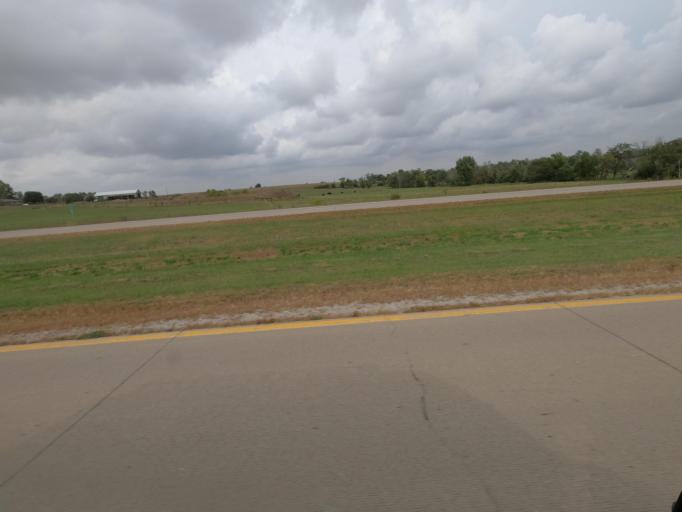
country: US
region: Iowa
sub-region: Wapello County
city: Ottumwa
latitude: 41.0026
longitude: -92.2771
